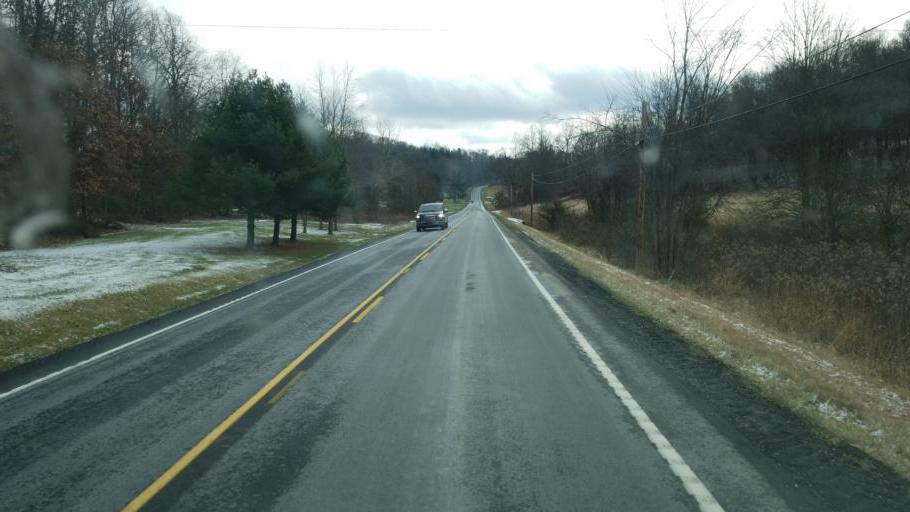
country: US
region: Ohio
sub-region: Muskingum County
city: Frazeysburg
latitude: 40.1238
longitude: -82.1910
